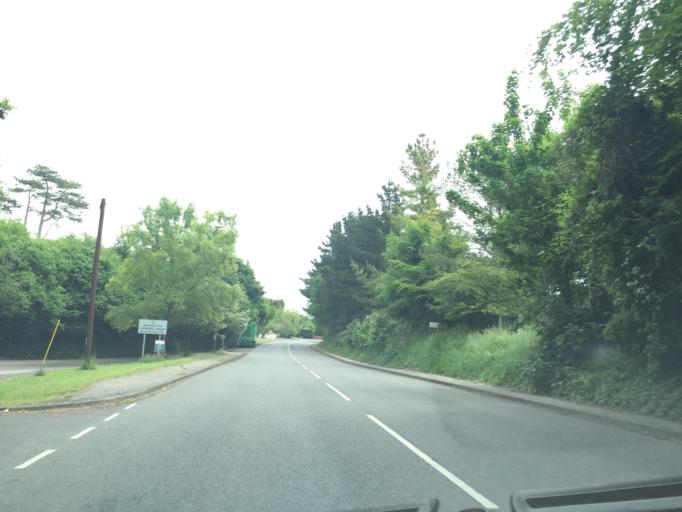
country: GB
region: England
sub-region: Dorset
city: Swanage
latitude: 50.6287
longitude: -1.9727
